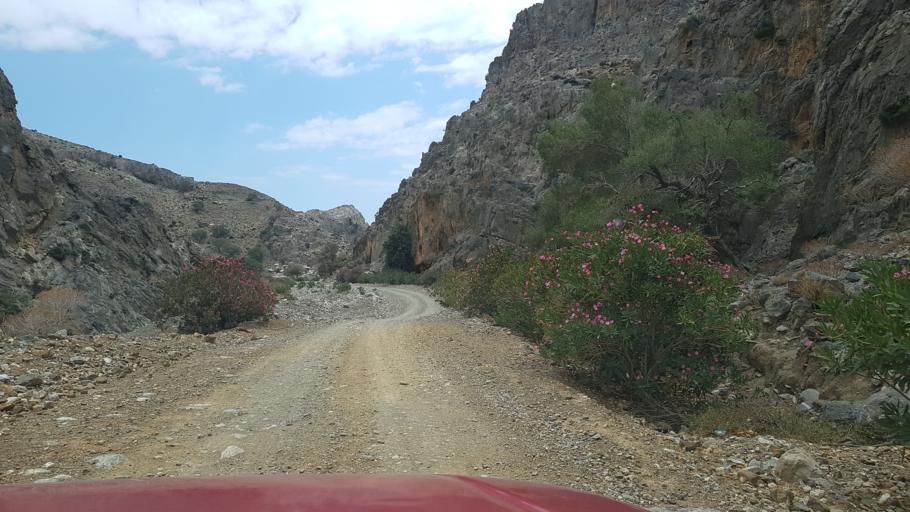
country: GR
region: Crete
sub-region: Nomos Irakleiou
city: Agioi Deka
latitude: 34.9410
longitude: 24.9843
